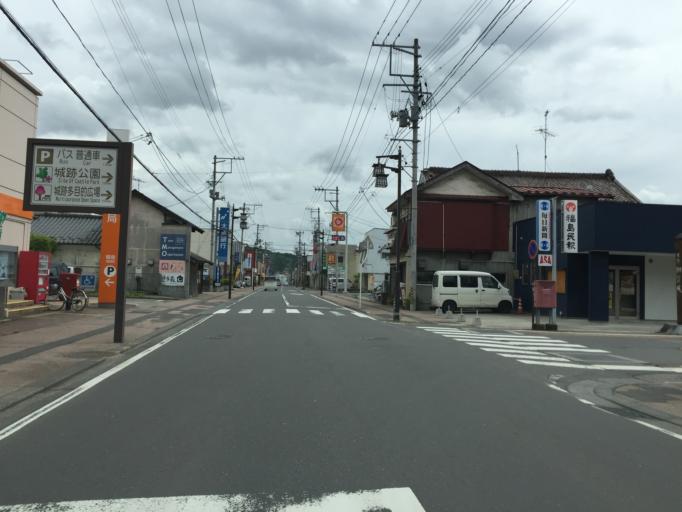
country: JP
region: Fukushima
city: Ishikawa
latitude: 37.0300
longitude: 140.3881
